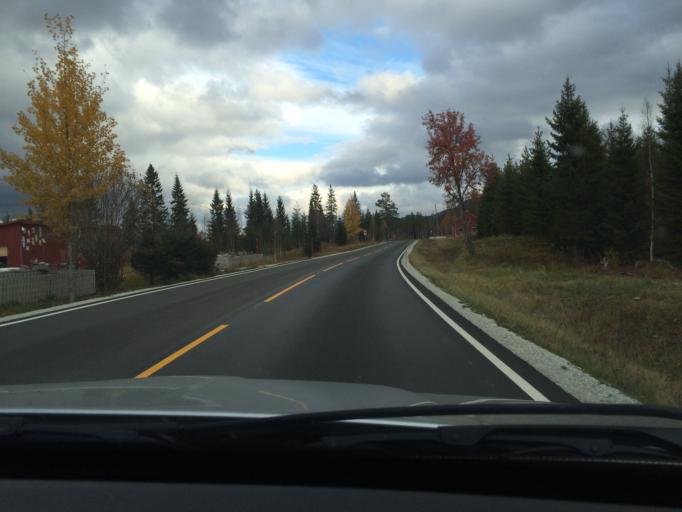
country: NO
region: Nord-Trondelag
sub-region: Namsskogan
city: Namsskogan
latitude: 64.7764
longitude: 12.8824
